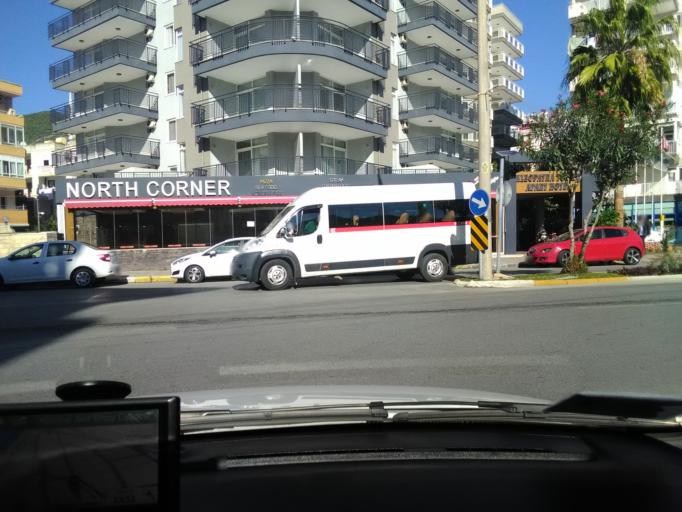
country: TR
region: Antalya
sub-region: Alanya
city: Alanya
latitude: 36.5512
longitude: 31.9864
